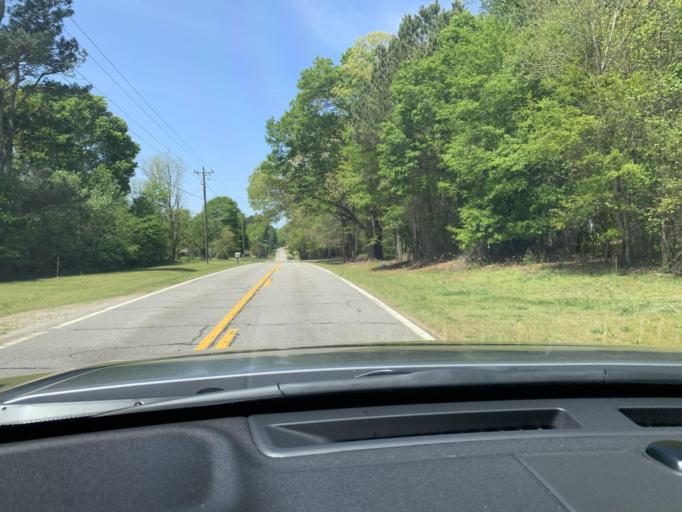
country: US
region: Georgia
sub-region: Barrow County
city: Statham
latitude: 33.9007
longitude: -83.6072
